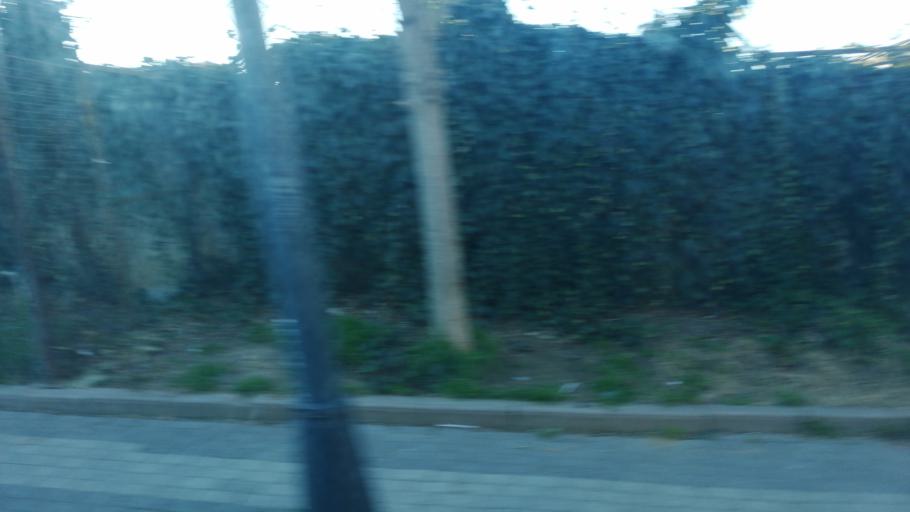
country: TR
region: Istanbul
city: UEskuedar
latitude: 41.0578
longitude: 29.0641
